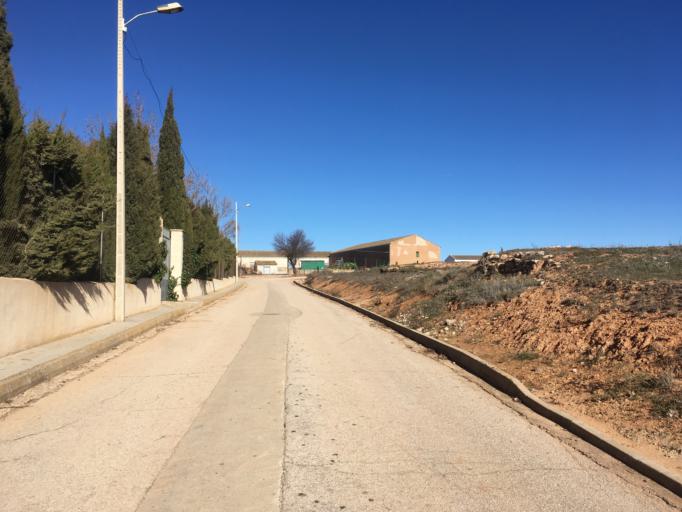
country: ES
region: Castille-La Mancha
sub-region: Provincia de Cuenca
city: Atalaya del Canavate
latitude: 39.5488
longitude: -2.2474
